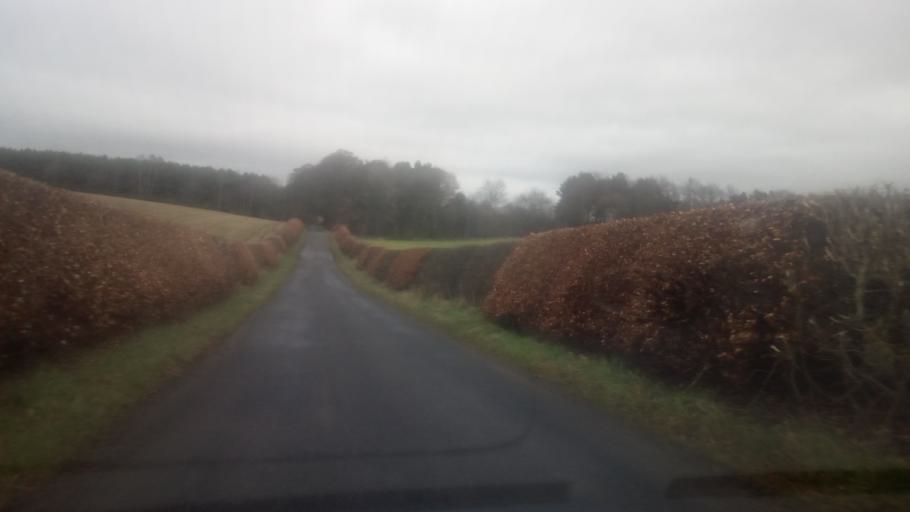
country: GB
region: Scotland
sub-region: The Scottish Borders
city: Jedburgh
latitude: 55.5376
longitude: -2.4967
